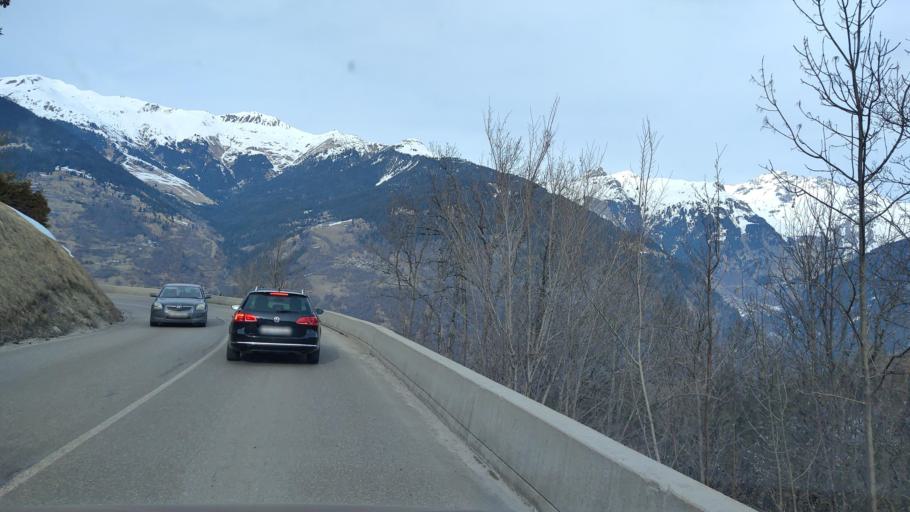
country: FR
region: Rhone-Alpes
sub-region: Departement de la Savoie
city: Saint-Bon-Tarentaise
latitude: 45.4267
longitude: 6.6397
